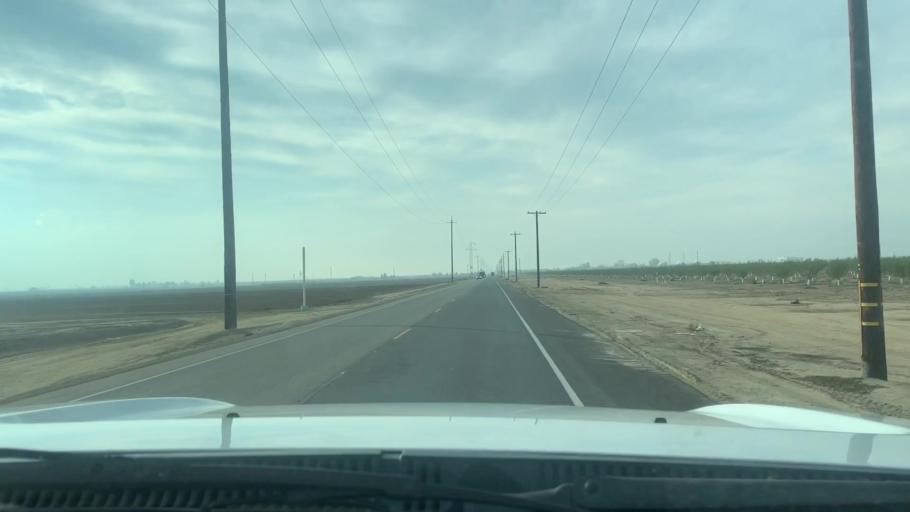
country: US
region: California
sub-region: Kern County
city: Shafter
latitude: 35.4417
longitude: -119.2293
